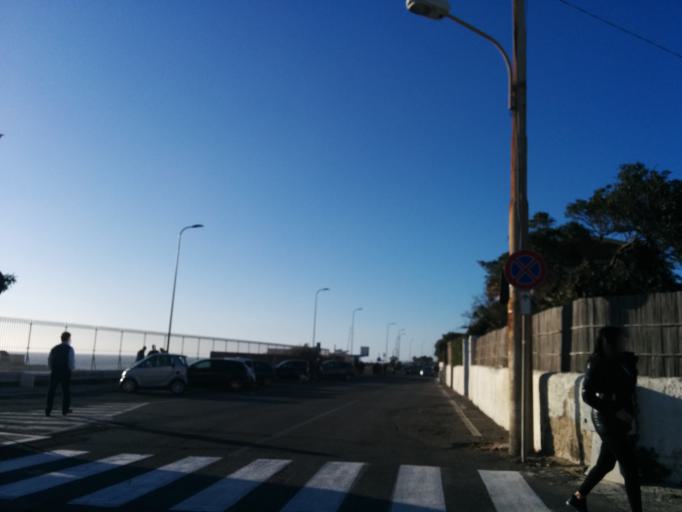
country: IT
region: Latium
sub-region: Citta metropolitana di Roma Capitale
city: Lavinio
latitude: 41.4972
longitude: 12.5854
